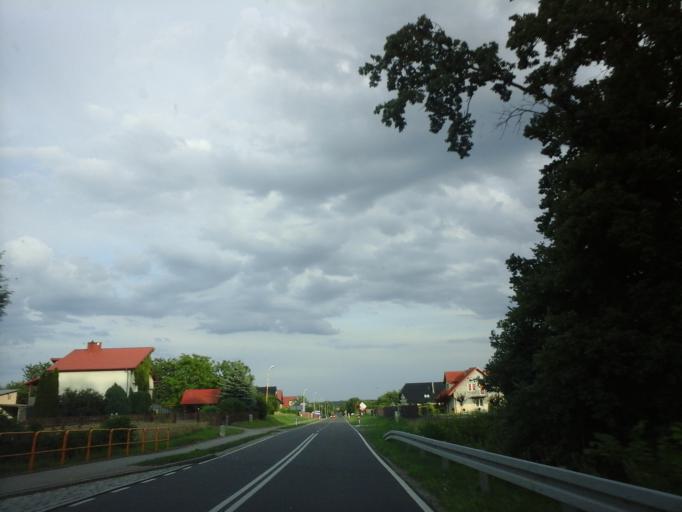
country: PL
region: West Pomeranian Voivodeship
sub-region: Powiat kamienski
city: Golczewo
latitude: 53.8334
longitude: 14.9630
